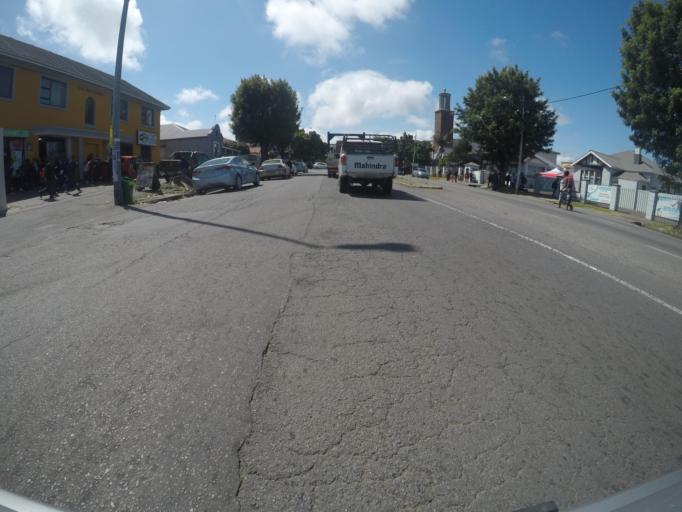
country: ZA
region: Eastern Cape
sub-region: Buffalo City Metropolitan Municipality
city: East London
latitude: -33.0033
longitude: 27.8997
